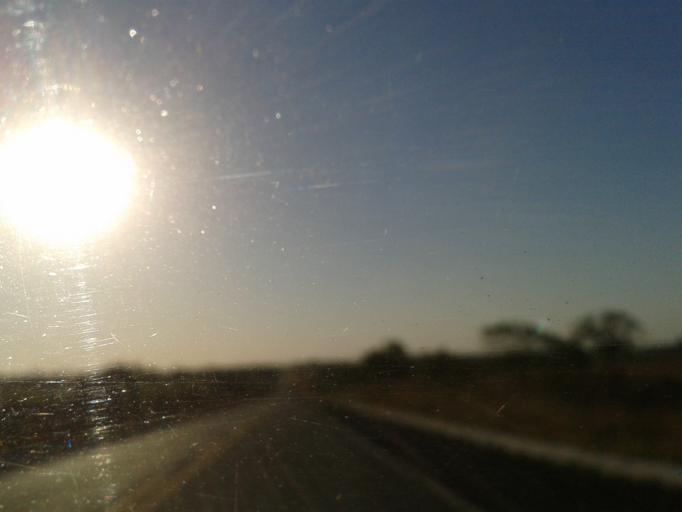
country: BR
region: Minas Gerais
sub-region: Santa Vitoria
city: Santa Vitoria
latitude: -19.0815
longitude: -50.3580
